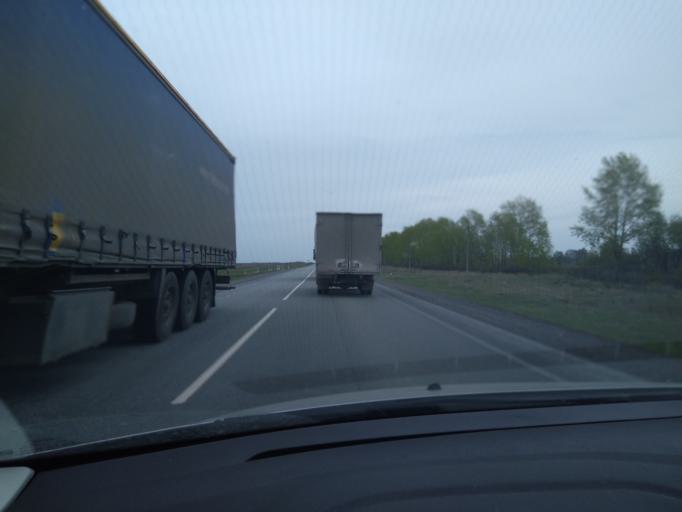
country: RU
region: Sverdlovsk
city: Talitsa
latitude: 57.0516
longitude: 63.5025
